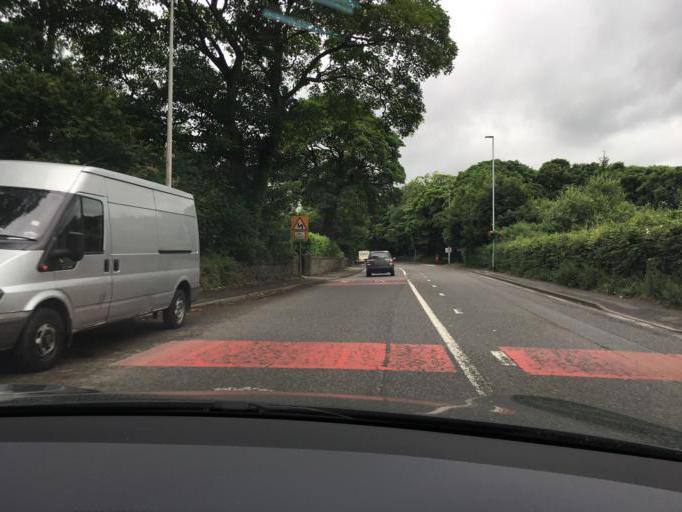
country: GB
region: England
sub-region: Derbyshire
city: New Mills
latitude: 53.3585
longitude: -2.0164
